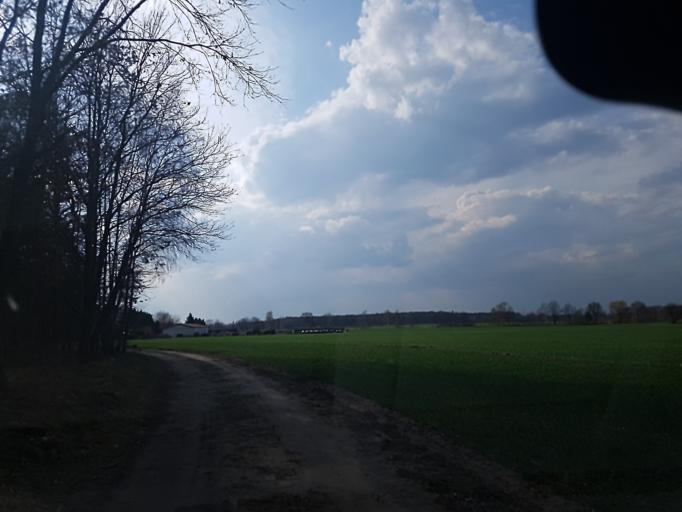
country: DE
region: Brandenburg
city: Schonewalde
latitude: 51.6383
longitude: 13.6159
